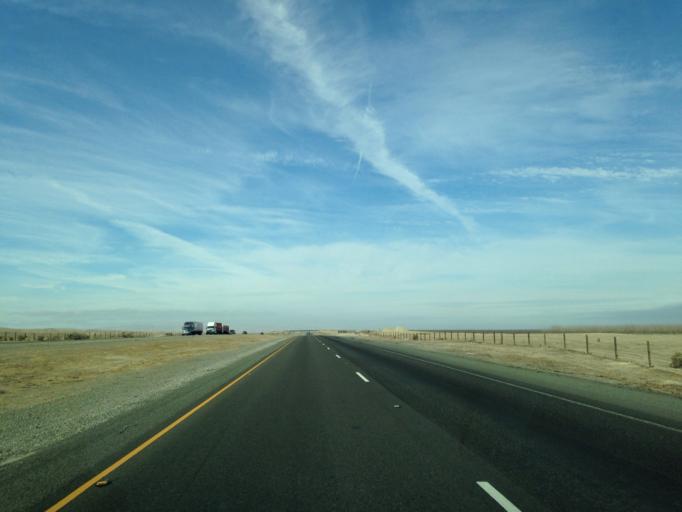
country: US
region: California
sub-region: Fresno County
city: Mendota
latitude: 36.5437
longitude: -120.5048
